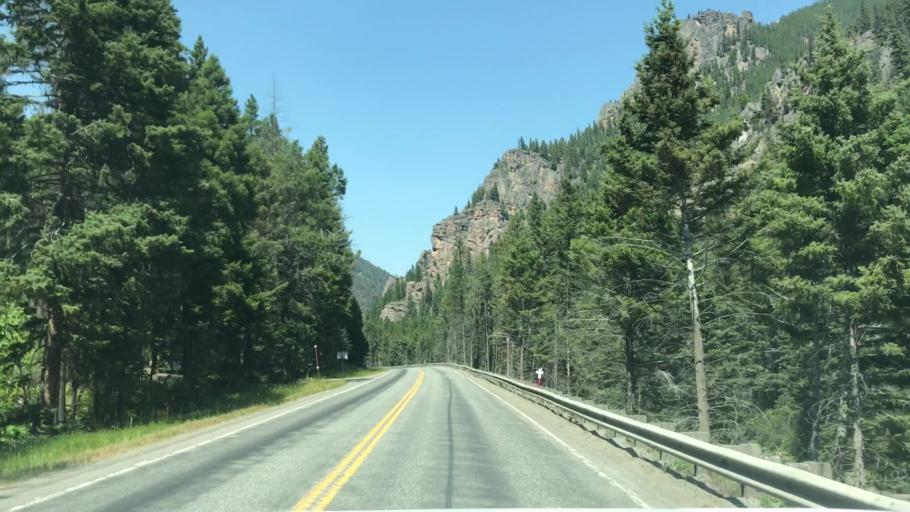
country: US
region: Montana
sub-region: Gallatin County
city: Big Sky
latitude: 45.4105
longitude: -111.2276
